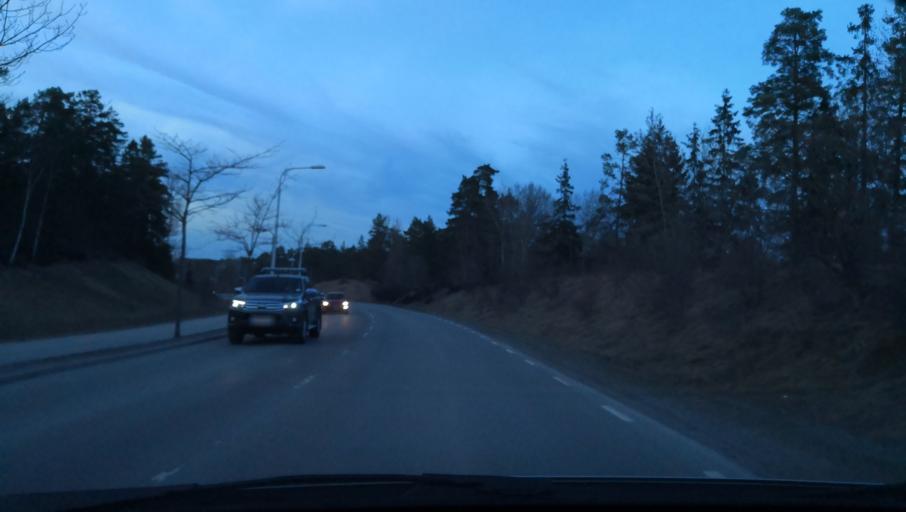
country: SE
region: Stockholm
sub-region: Varmdo Kommun
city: Gustavsberg
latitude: 59.3140
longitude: 18.3909
